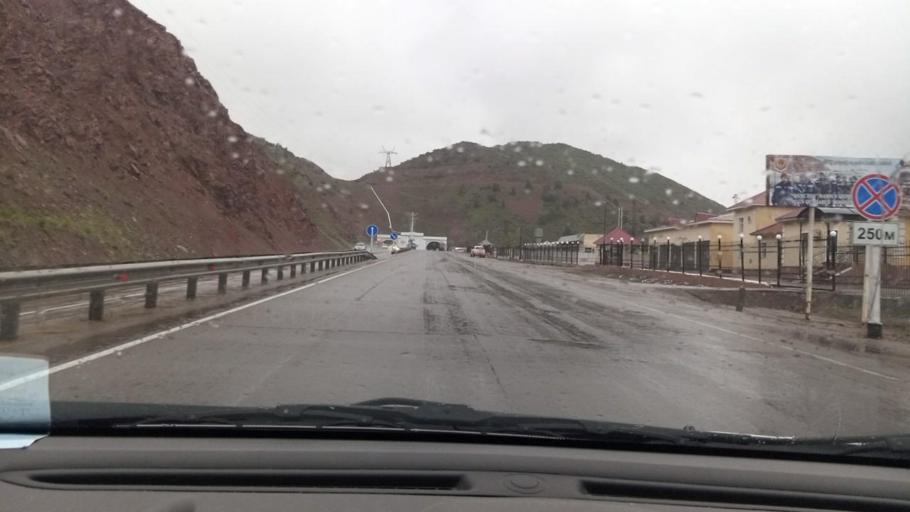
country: UZ
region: Toshkent
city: Angren
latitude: 41.0826
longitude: 70.5432
